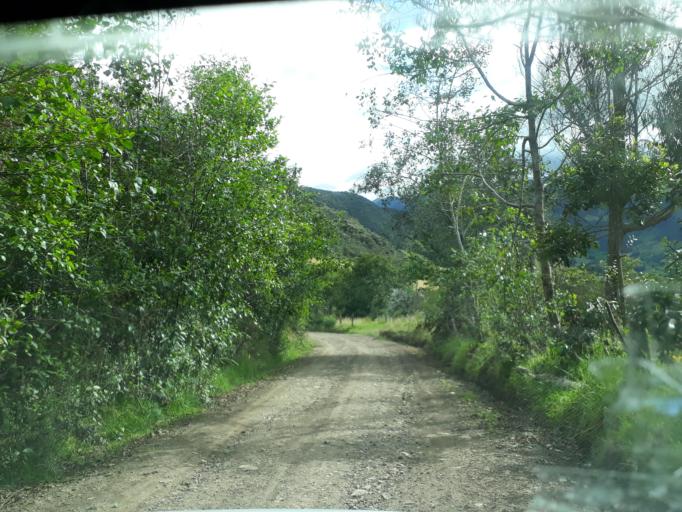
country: CO
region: Cundinamarca
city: La Mesa
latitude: 5.2642
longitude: -73.8958
